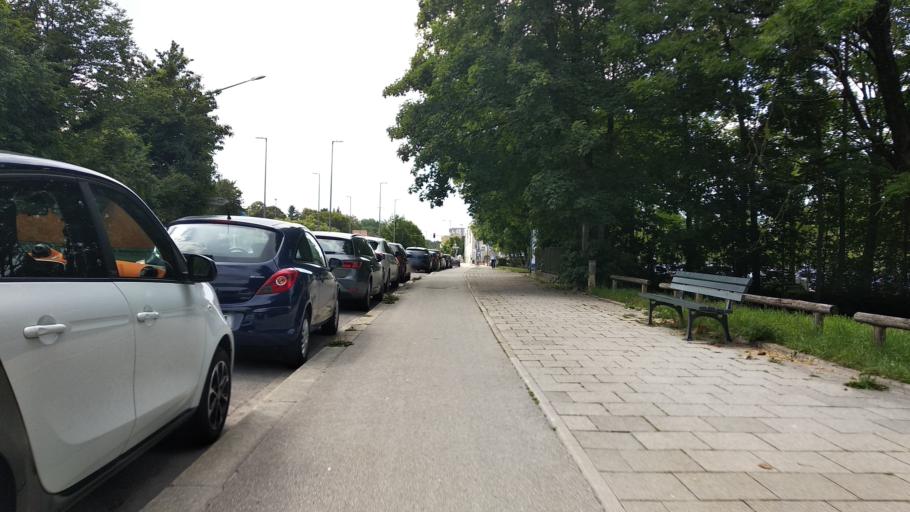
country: DE
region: Bavaria
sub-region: Upper Bavaria
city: Bogenhausen
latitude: 48.1185
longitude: 11.6326
